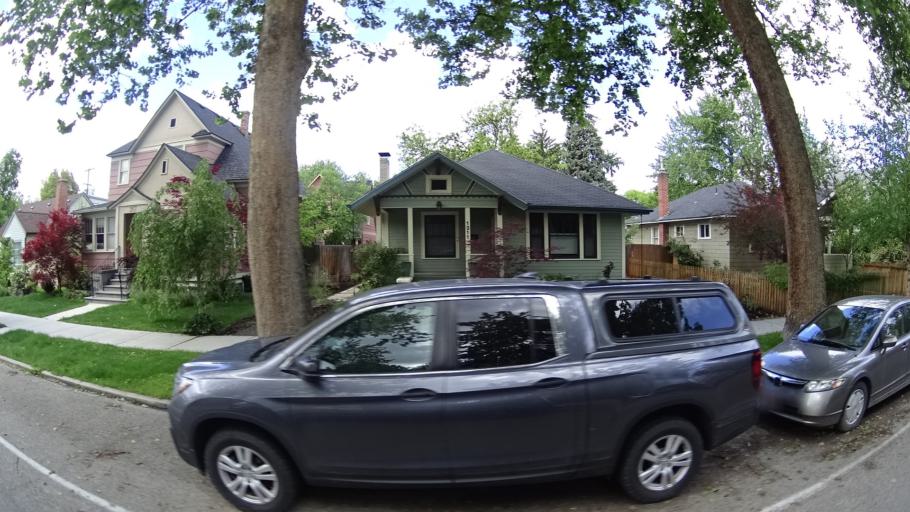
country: US
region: Idaho
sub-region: Ada County
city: Boise
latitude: 43.6289
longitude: -116.2059
